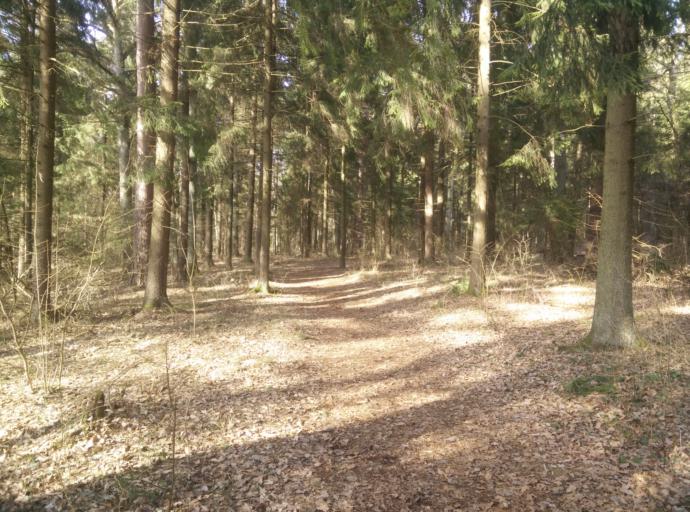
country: LT
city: Trakai
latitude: 54.6415
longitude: 24.9794
